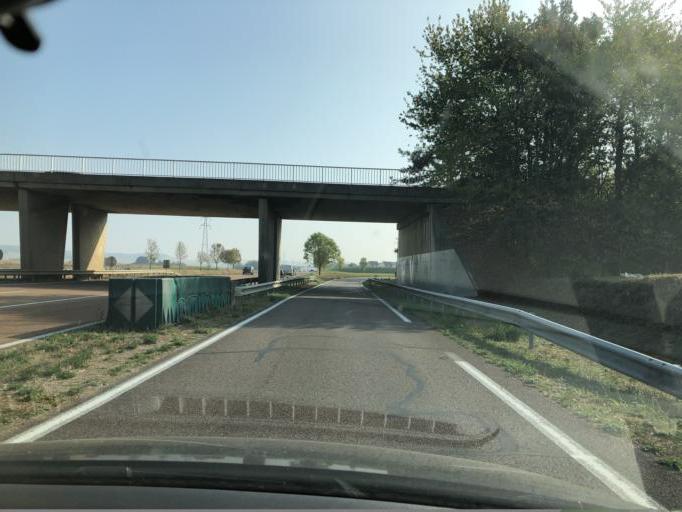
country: FR
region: Bourgogne
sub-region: Departement de l'Yonne
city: Saint-Clement
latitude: 48.2240
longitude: 3.2876
